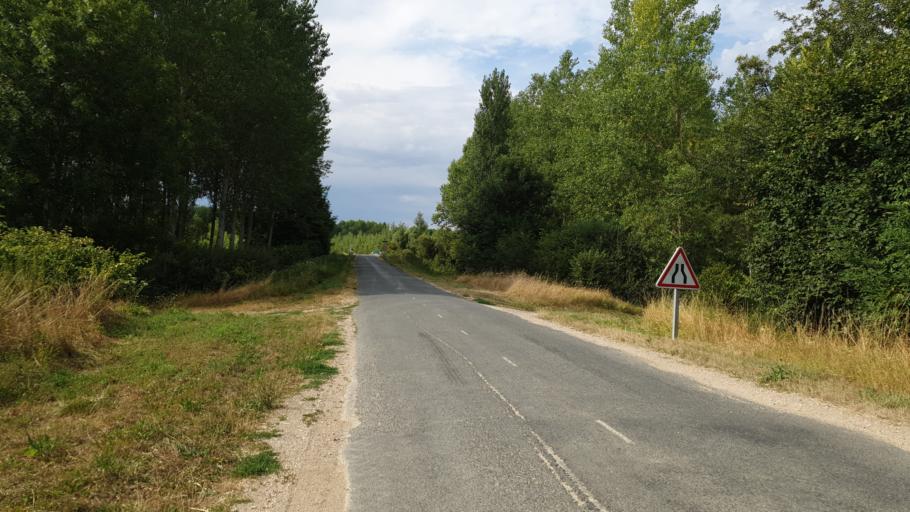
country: FR
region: Champagne-Ardenne
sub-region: Departement de la Marne
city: Pargny-sur-Saulx
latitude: 48.7642
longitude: 4.7499
